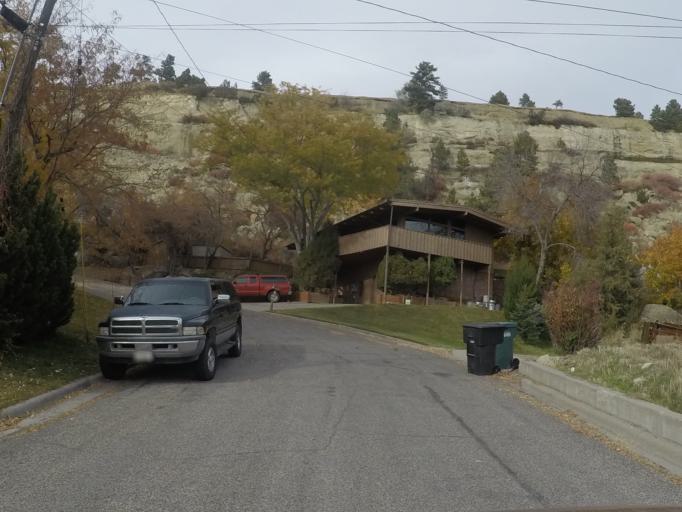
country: US
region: Montana
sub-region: Yellowstone County
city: Billings
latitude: 45.8008
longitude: -108.5488
